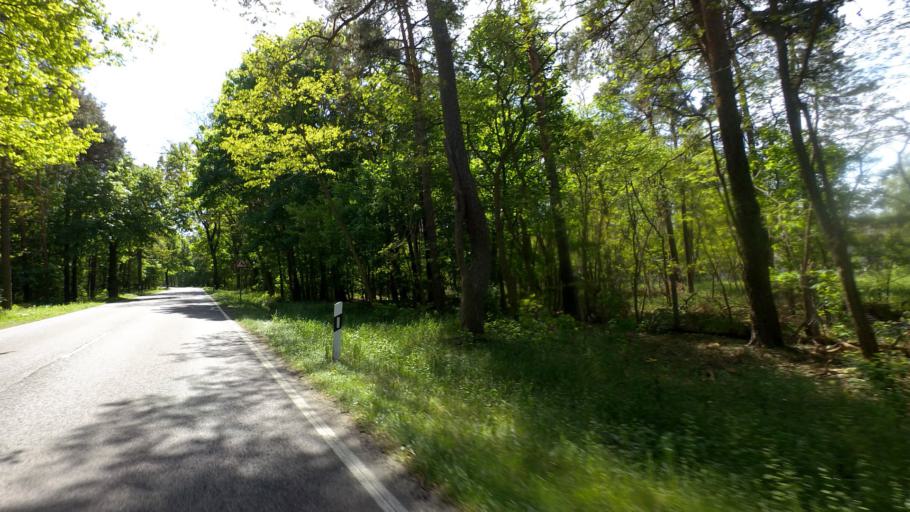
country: DE
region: Brandenburg
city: Luckenwalde
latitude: 52.1580
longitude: 13.1023
